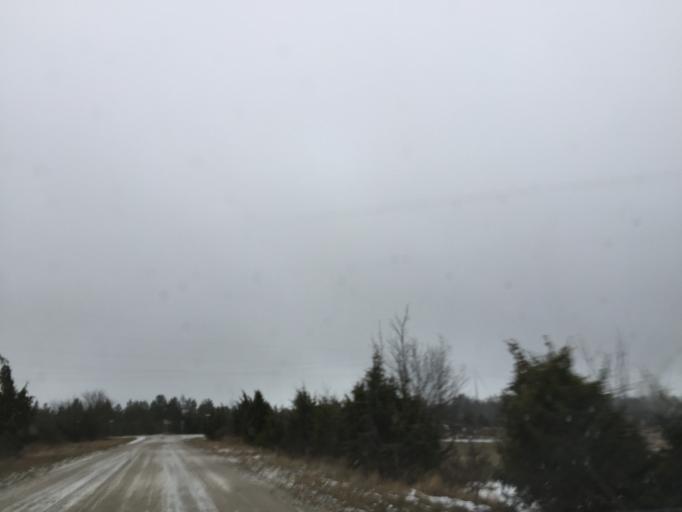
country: EE
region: Laeaene
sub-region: Lihula vald
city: Lihula
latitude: 58.5756
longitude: 23.5421
